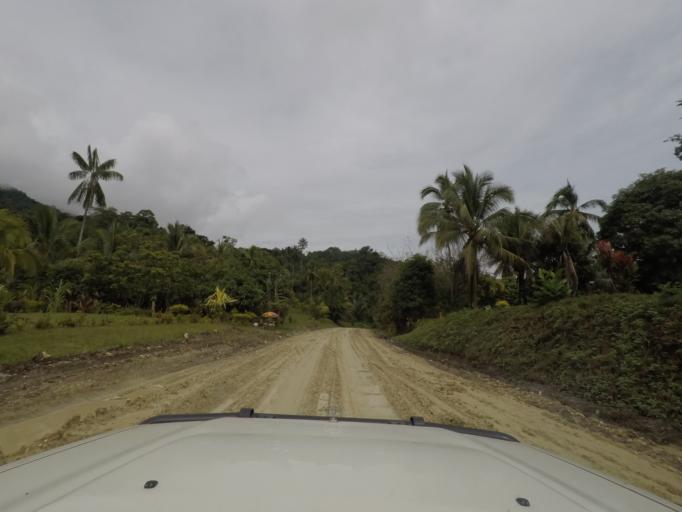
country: PG
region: Madang
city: Madang
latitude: -5.5017
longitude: 145.4516
